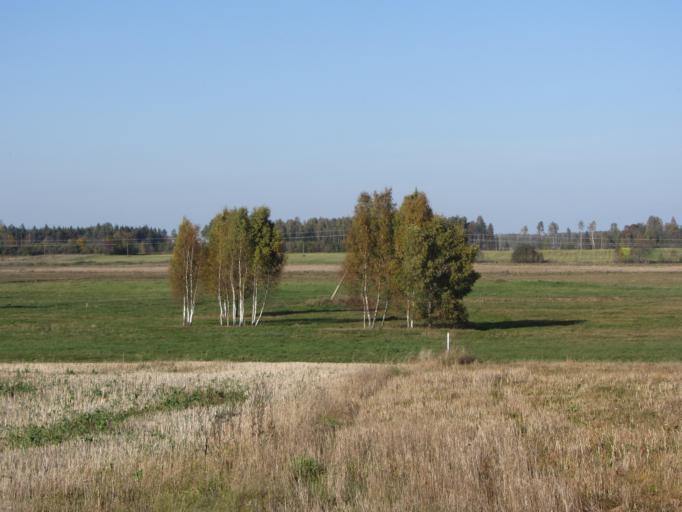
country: LT
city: Obeliai
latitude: 55.9814
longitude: 25.3317
